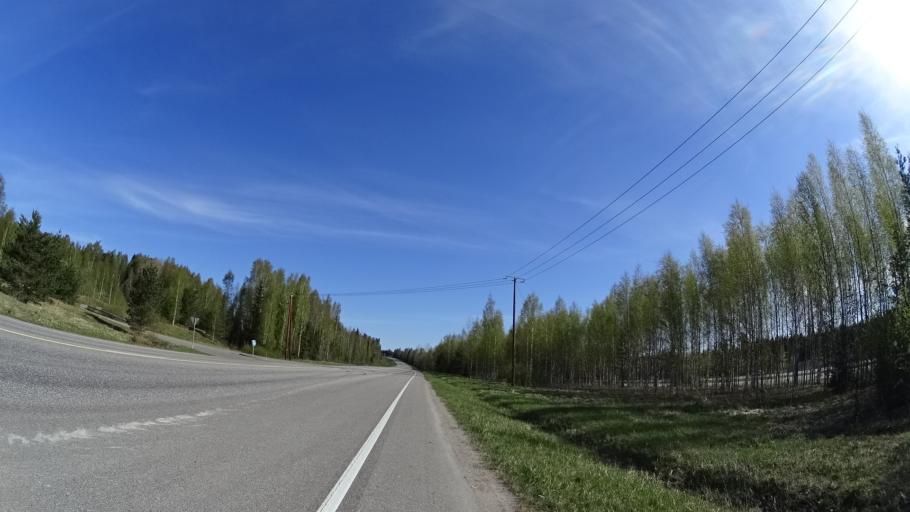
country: FI
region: Uusimaa
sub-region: Helsinki
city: Nurmijaervi
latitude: 60.4064
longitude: 24.8203
